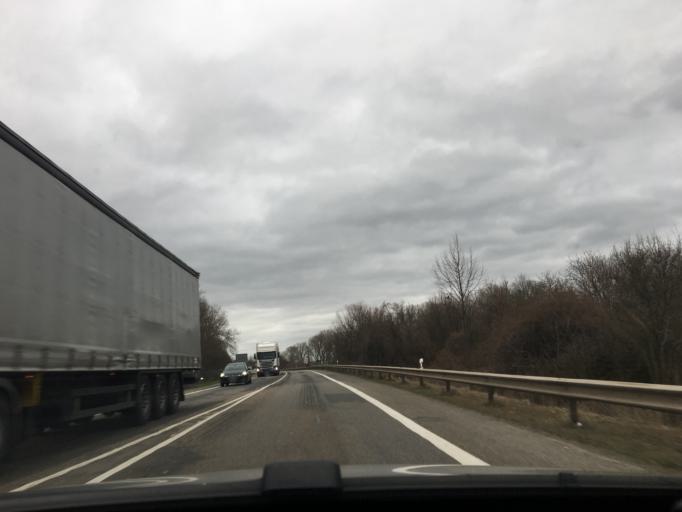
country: DE
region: Rheinland-Pfalz
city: Worms
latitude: 49.6727
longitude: 8.3543
